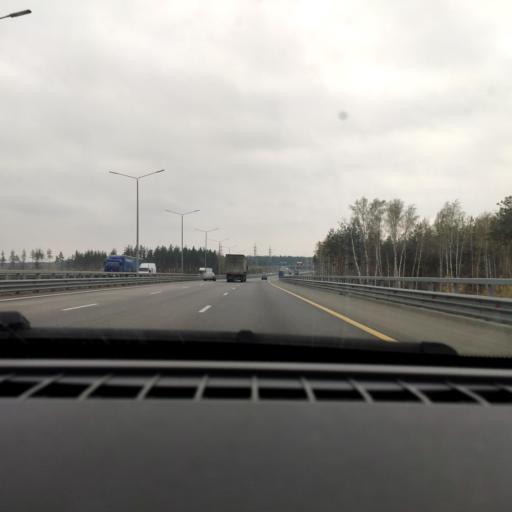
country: RU
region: Voronezj
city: Somovo
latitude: 51.7329
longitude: 39.3101
